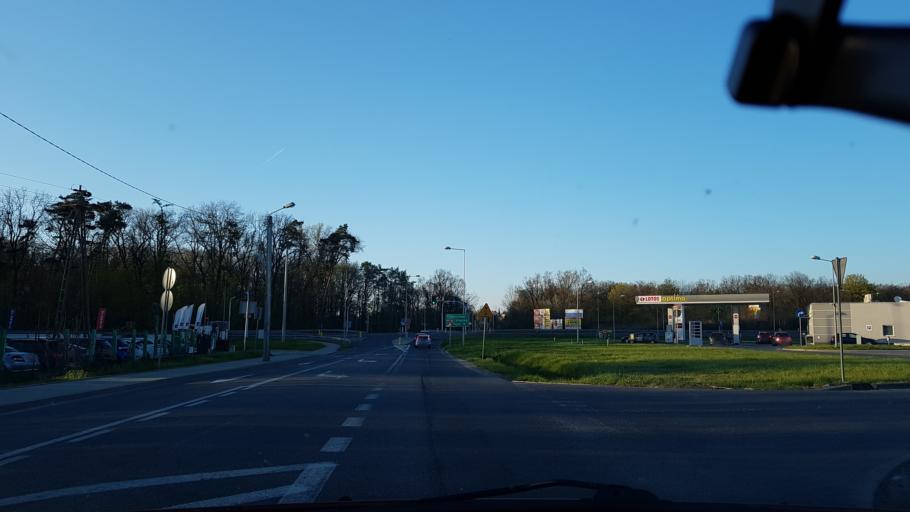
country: PL
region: Opole Voivodeship
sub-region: Powiat nyski
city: Otmuchow
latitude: 50.4570
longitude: 17.1669
